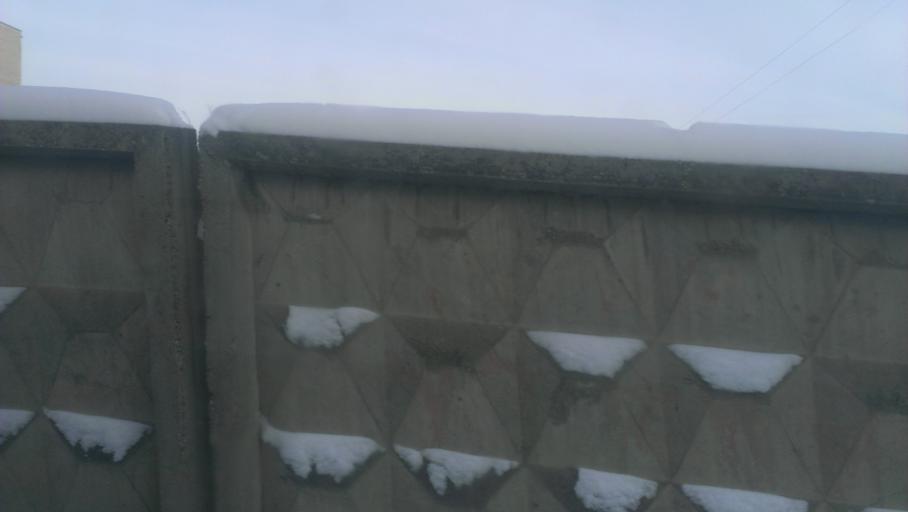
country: RU
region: Altai Krai
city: Nauchnyy Gorodok
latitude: 53.4215
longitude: 83.5214
